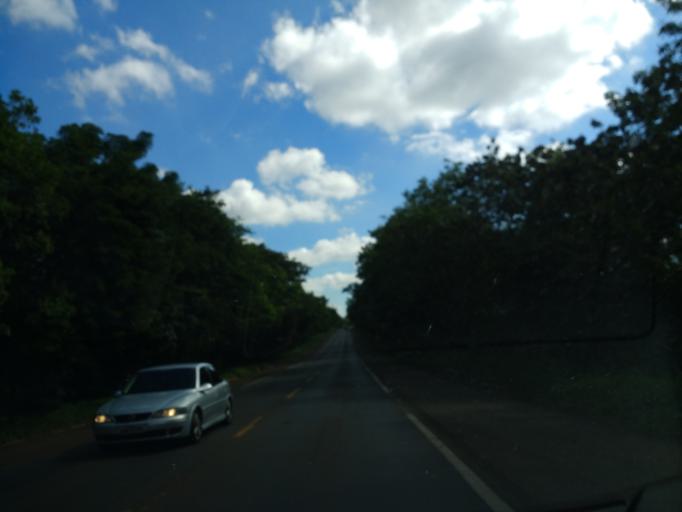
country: BR
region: Parana
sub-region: Alto Piquiri
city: Alto Piquiri
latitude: -23.8922
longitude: -53.4399
